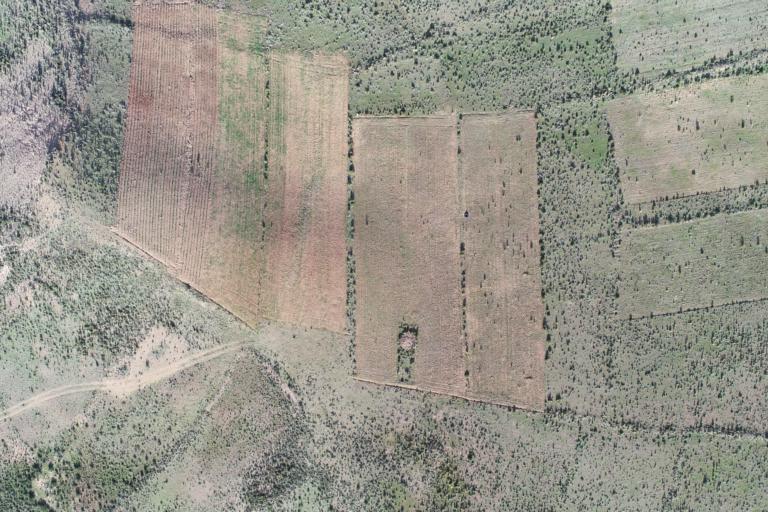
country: BO
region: La Paz
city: Curahuara de Carangas
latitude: -17.2990
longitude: -68.4940
